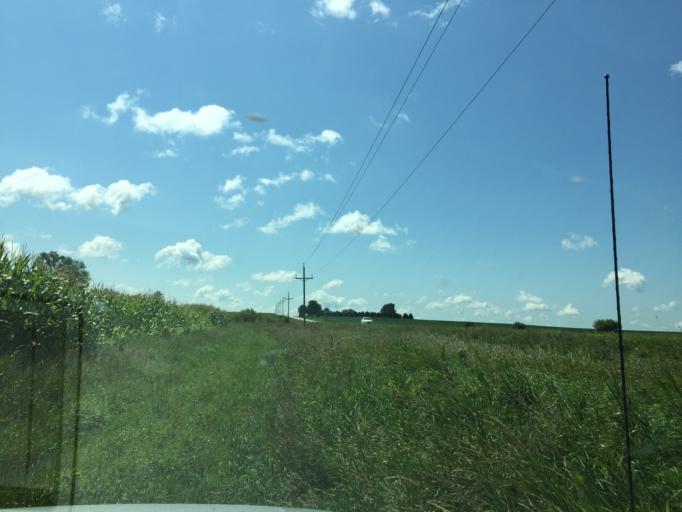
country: US
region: Minnesota
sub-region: Olmsted County
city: Byron
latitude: 44.0025
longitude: -92.6081
